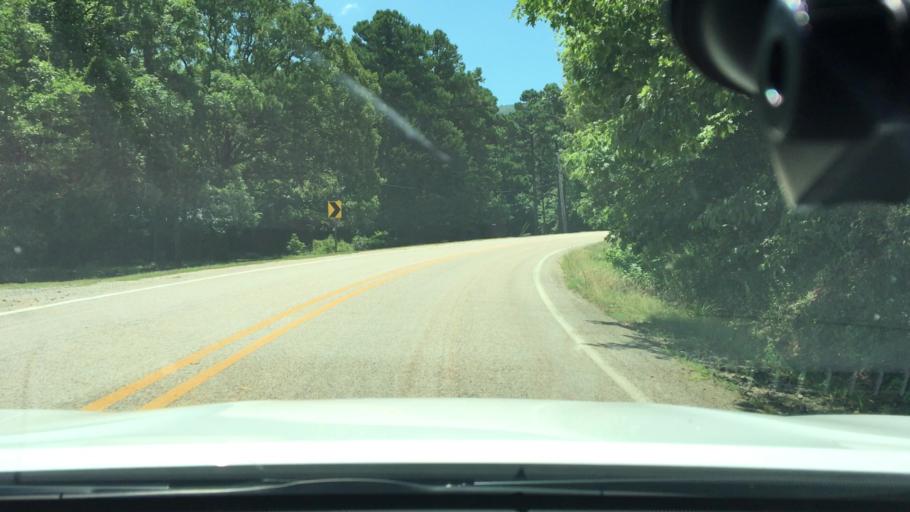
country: US
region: Arkansas
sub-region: Logan County
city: Paris
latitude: 35.1901
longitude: -93.6227
